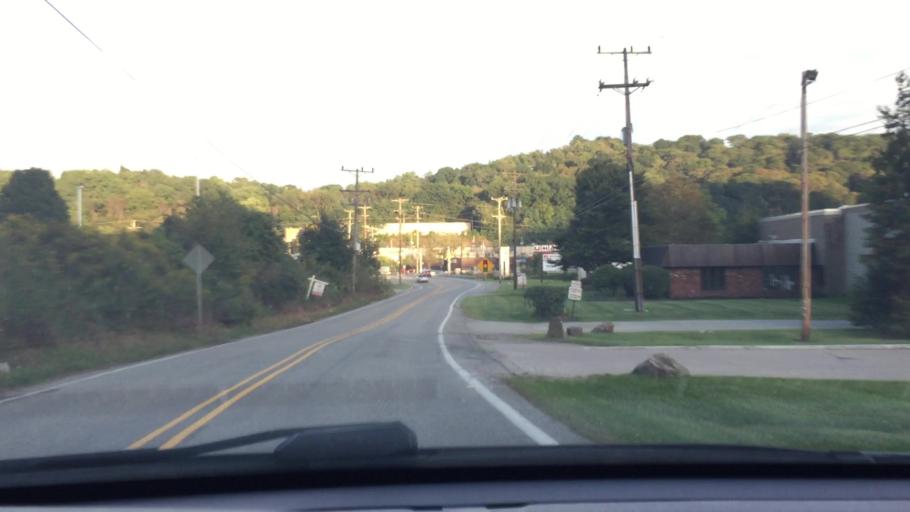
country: US
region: Pennsylvania
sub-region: Westmoreland County
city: Murrysville
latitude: 40.4464
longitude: -79.7164
